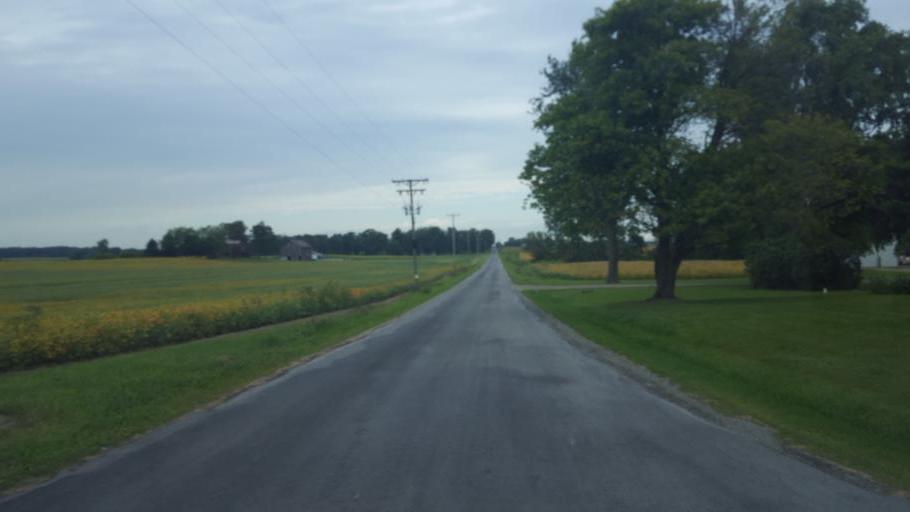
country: US
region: Ohio
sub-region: Wyandot County
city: Upper Sandusky
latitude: 40.8407
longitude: -83.1890
